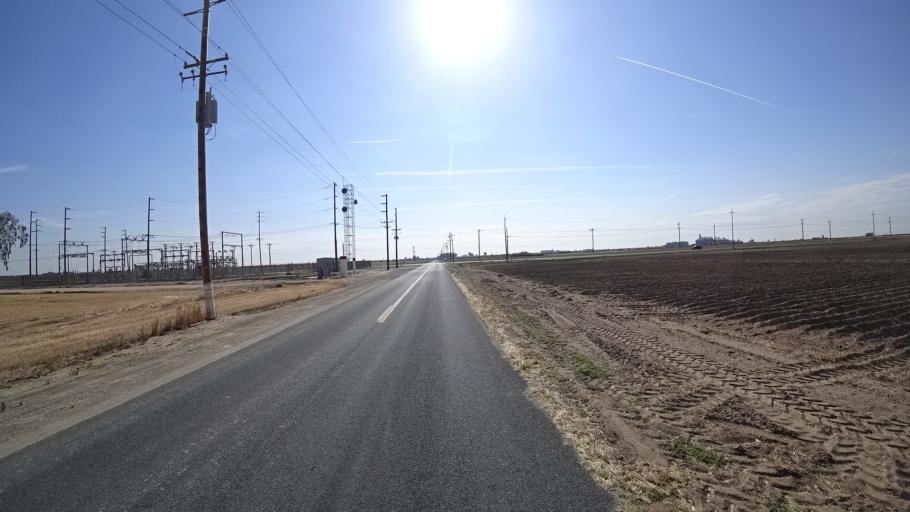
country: US
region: California
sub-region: Kings County
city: Home Garden
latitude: 36.2258
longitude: -119.6565
